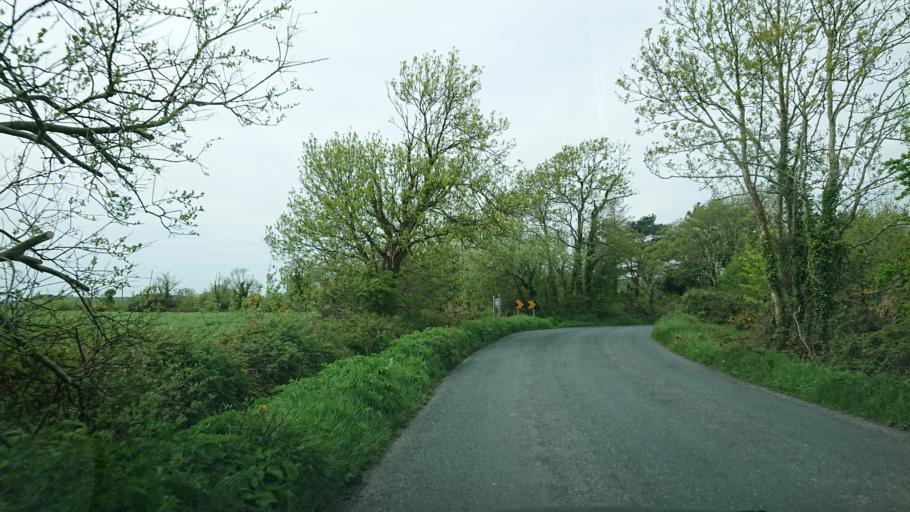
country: IE
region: Munster
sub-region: Waterford
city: Waterford
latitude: 52.2066
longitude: -7.0947
